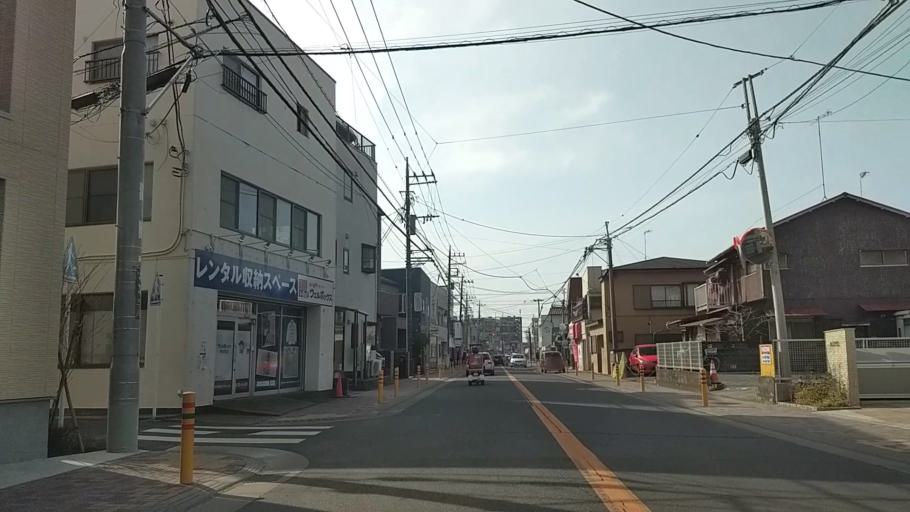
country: JP
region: Kanagawa
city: Chigasaki
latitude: 35.3329
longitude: 139.4211
